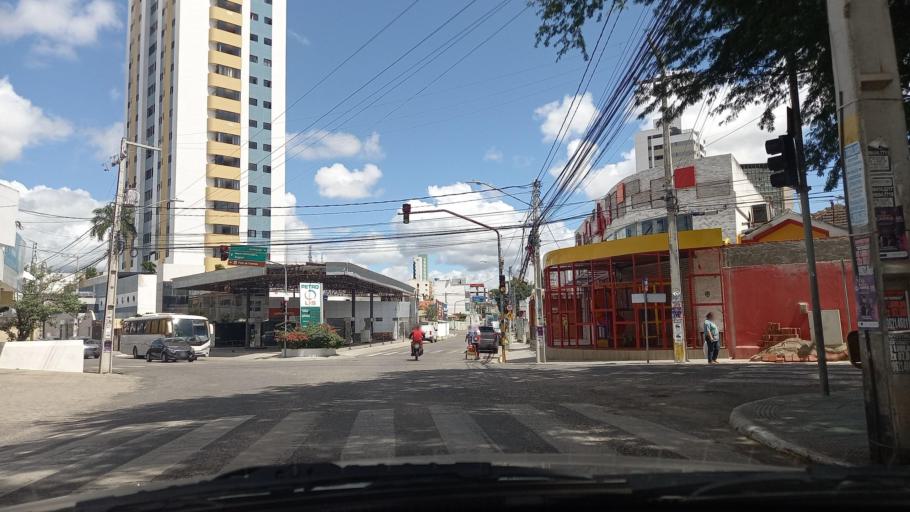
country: BR
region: Pernambuco
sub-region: Caruaru
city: Caruaru
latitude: -8.2772
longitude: -35.9677
